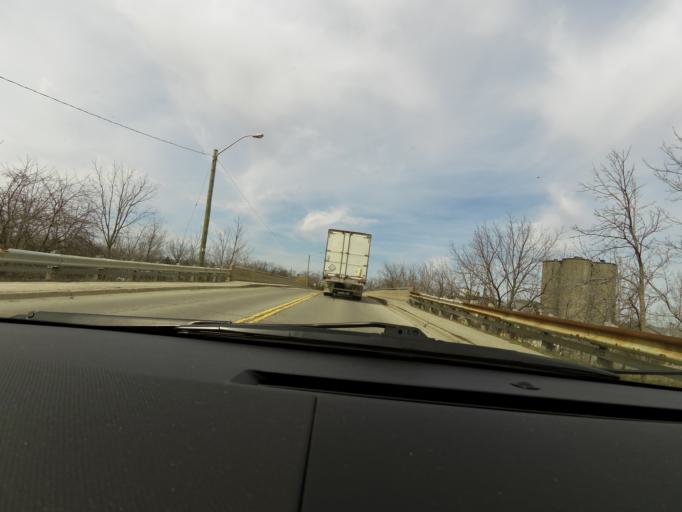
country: CA
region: Ontario
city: Ancaster
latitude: 42.9564
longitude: -79.8585
